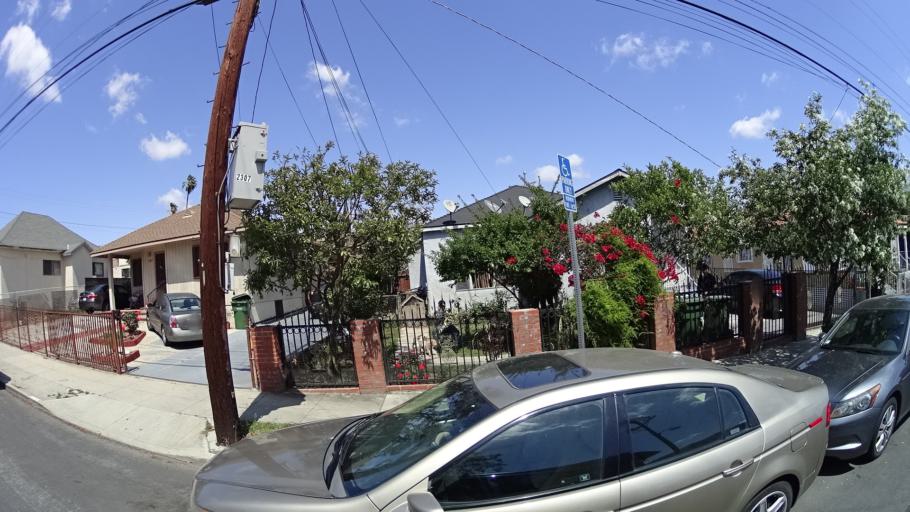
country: US
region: California
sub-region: Los Angeles County
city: Boyle Heights
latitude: 34.0506
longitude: -118.2073
